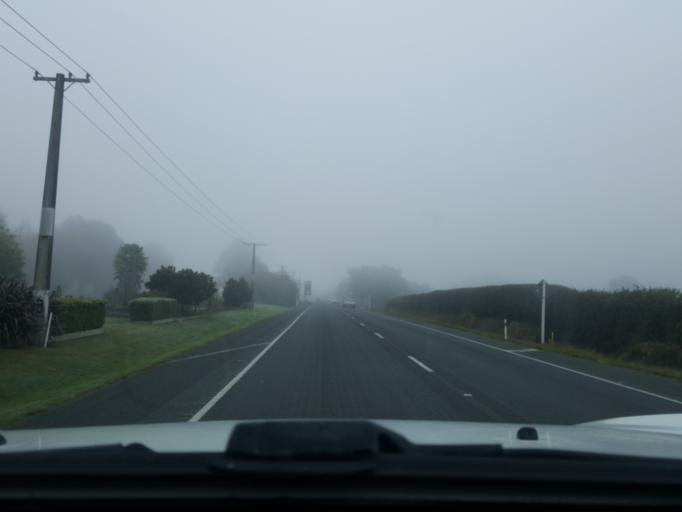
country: NZ
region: Waikato
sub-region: Waikato District
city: Ngaruawahia
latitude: -37.6808
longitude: 175.1668
